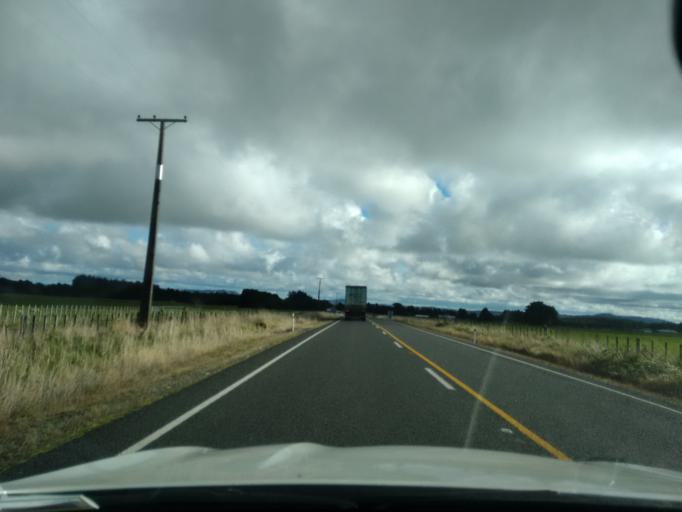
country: NZ
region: Manawatu-Wanganui
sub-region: Ruapehu District
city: Waiouru
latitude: -39.3559
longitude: 175.3538
